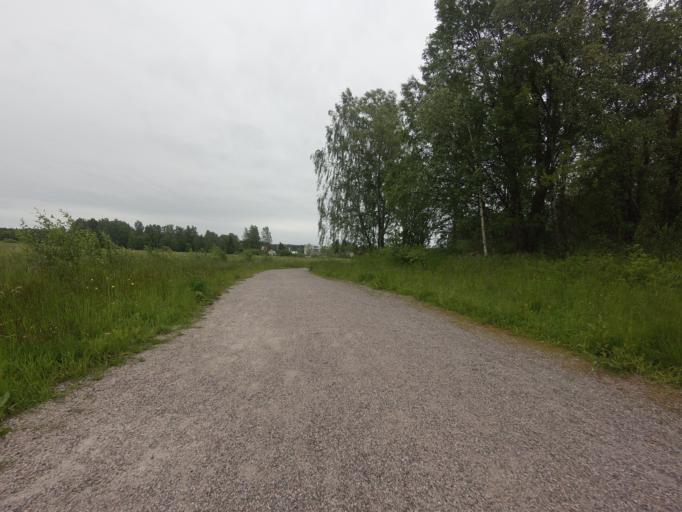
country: FI
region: Uusimaa
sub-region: Helsinki
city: Kauniainen
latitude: 60.1865
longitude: 24.7312
